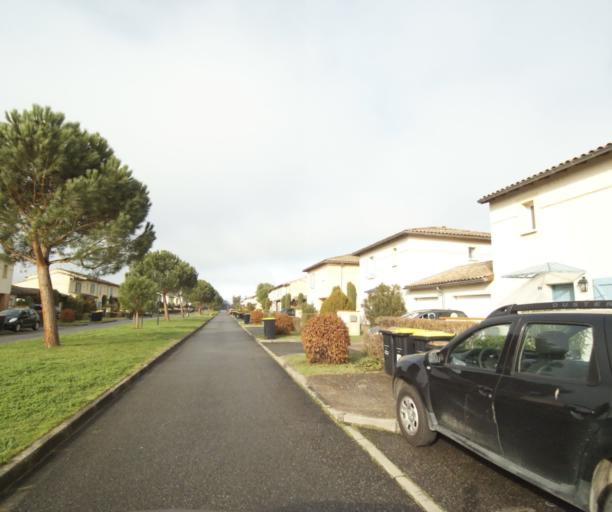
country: FR
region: Midi-Pyrenees
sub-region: Departement de la Haute-Garonne
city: Villemur-sur-Tarn
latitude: 43.8576
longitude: 1.4991
